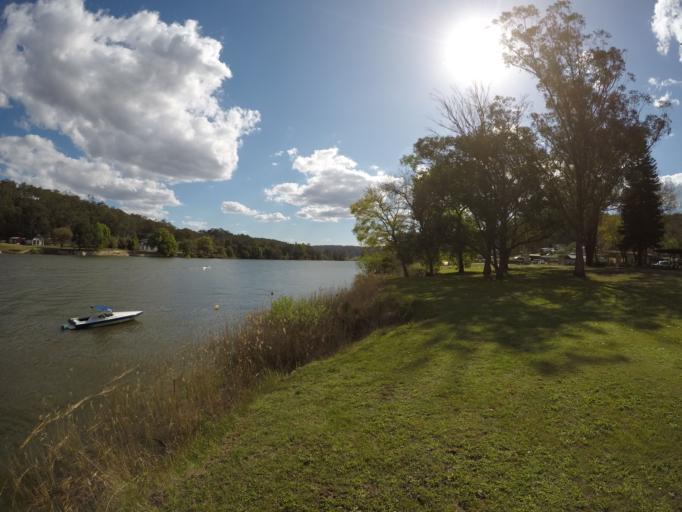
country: AU
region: New South Wales
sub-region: Hawkesbury
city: Pitt Town
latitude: -33.4730
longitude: 150.8929
